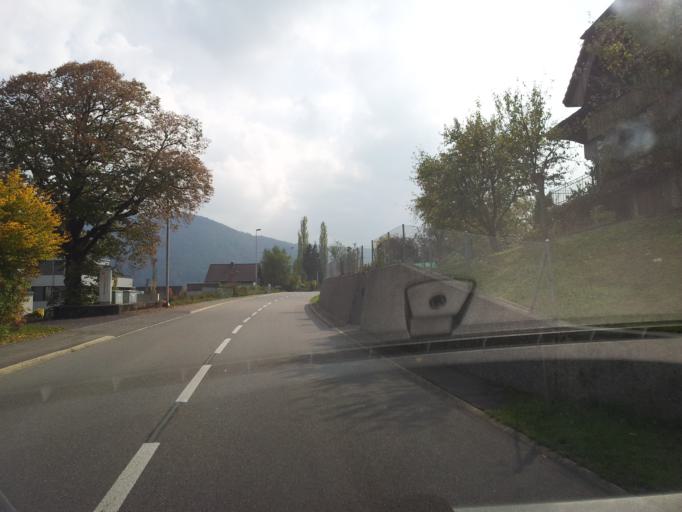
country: CH
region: Bern
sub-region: Bern-Mittelland District
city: Belp
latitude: 46.8913
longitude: 7.4941
